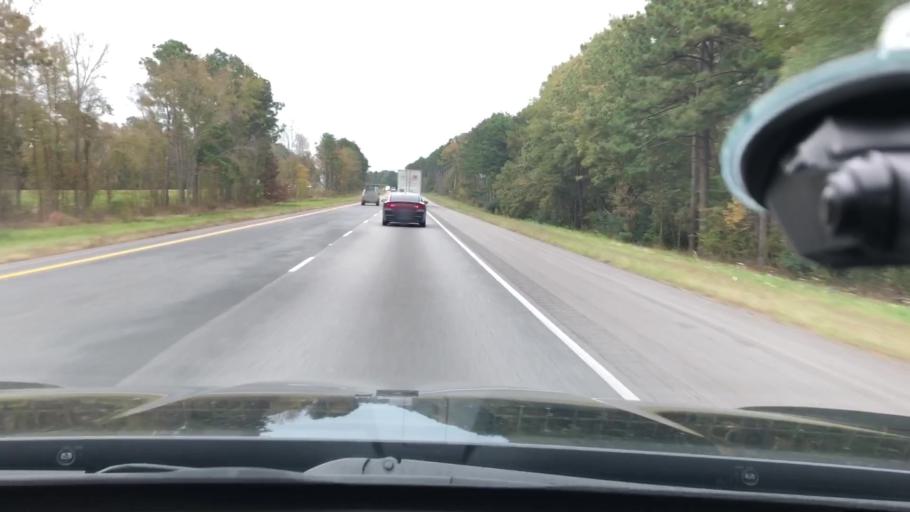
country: US
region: Arkansas
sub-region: Hempstead County
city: Hope
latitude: 33.6279
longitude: -93.7378
